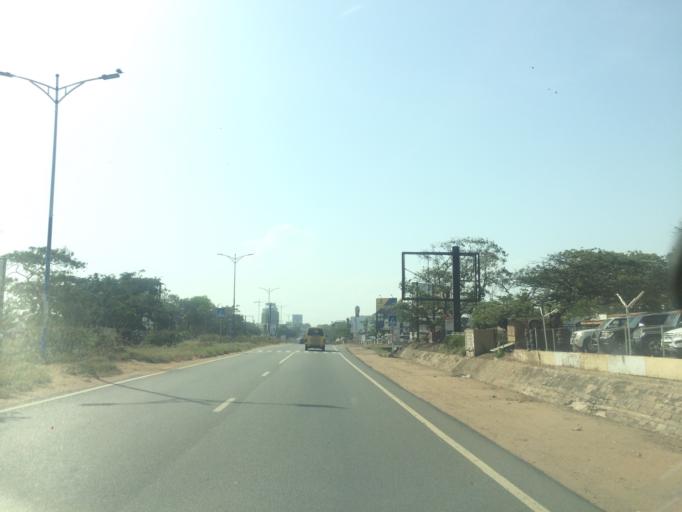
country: GH
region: Greater Accra
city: Accra
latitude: 5.5620
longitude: -0.1718
